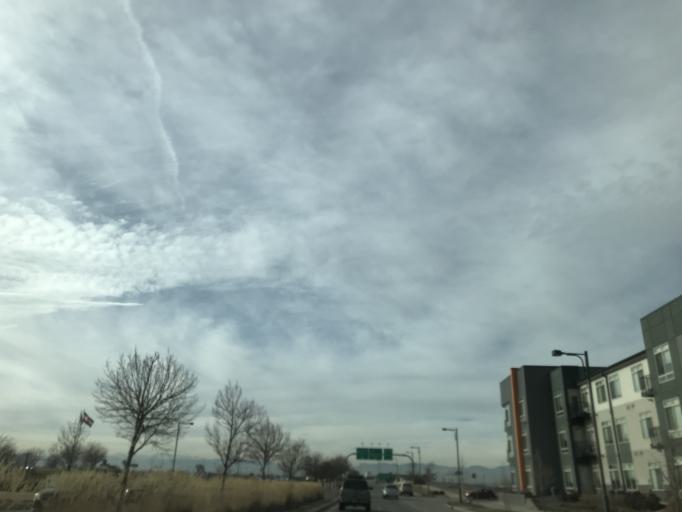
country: US
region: Colorado
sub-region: Adams County
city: Commerce City
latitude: 39.7856
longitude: -104.8953
